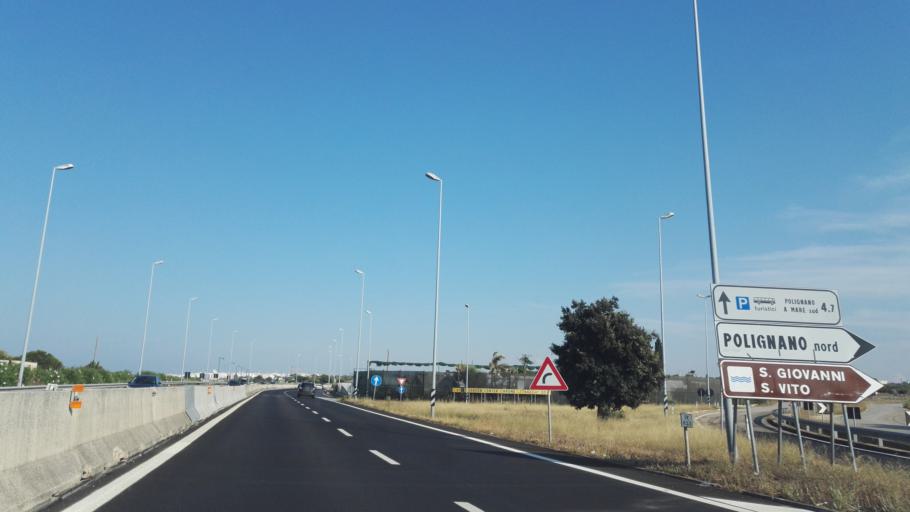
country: IT
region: Apulia
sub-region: Provincia di Bari
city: Polignano a Mare
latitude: 41.0068
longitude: 17.1931
